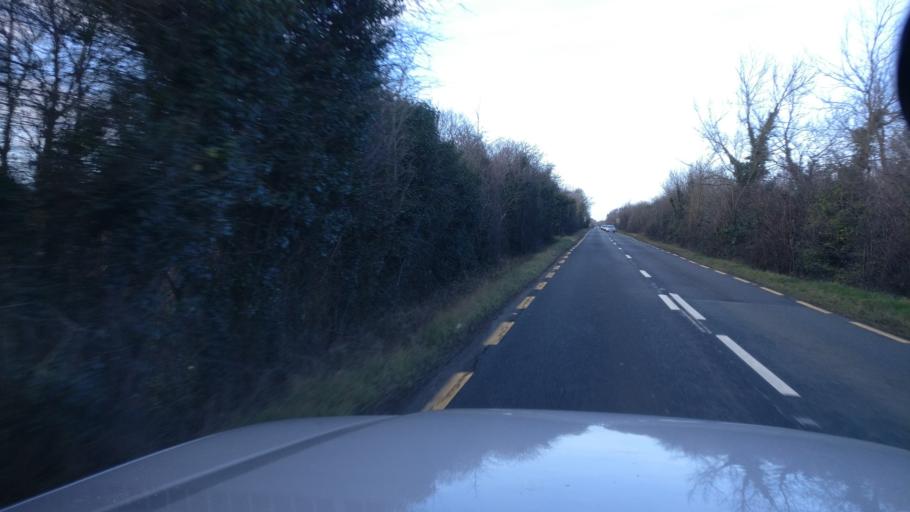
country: IE
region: Leinster
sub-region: Laois
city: Portlaoise
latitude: 53.0694
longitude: -7.3277
